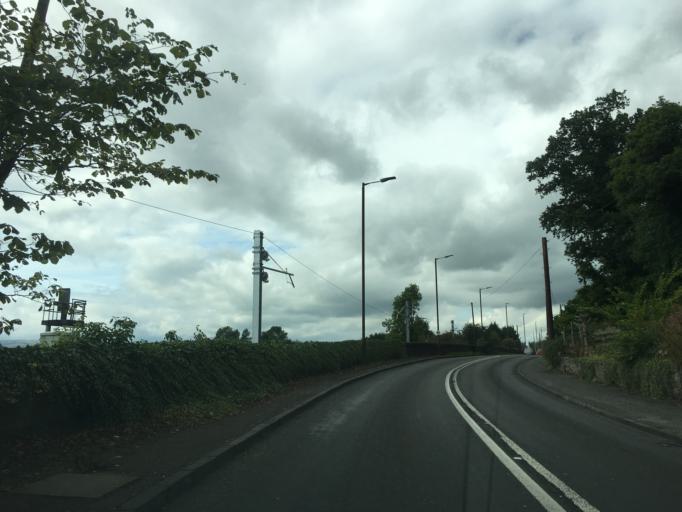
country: GB
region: Scotland
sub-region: Stirling
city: Stirling
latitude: 56.1335
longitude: -3.9108
